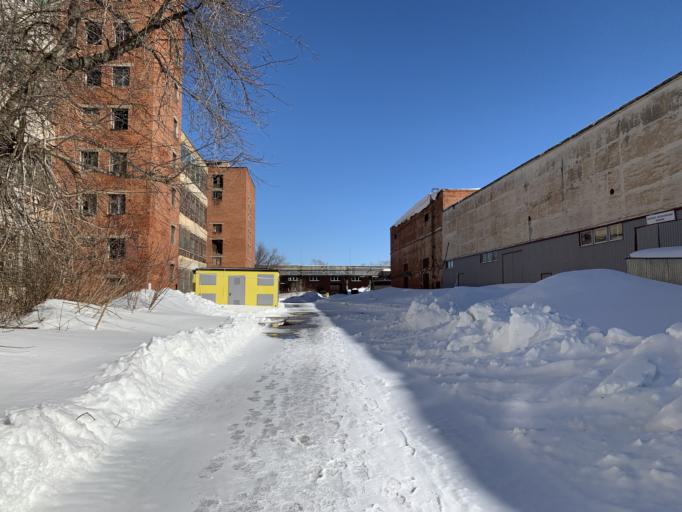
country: RU
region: Chuvashia
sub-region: Cheboksarskiy Rayon
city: Cheboksary
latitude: 56.1409
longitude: 47.2764
